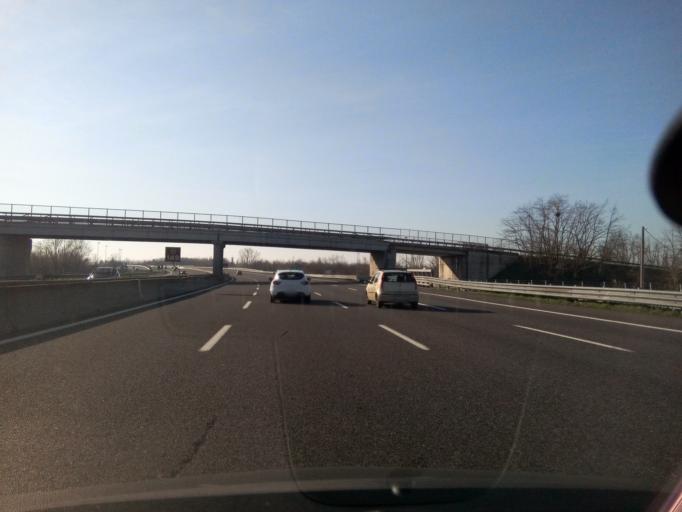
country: IT
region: Emilia-Romagna
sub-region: Provincia di Modena
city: Baggiovara
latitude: 44.6218
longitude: 10.8825
